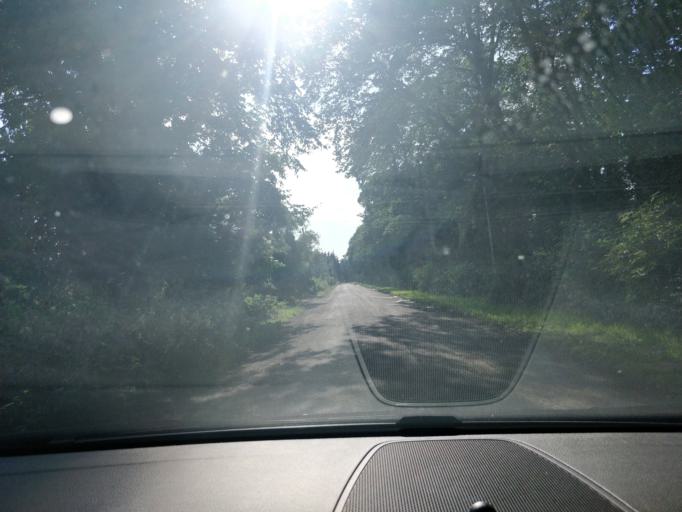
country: GB
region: England
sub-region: Lancashire
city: Banks
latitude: 53.6663
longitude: -2.9151
